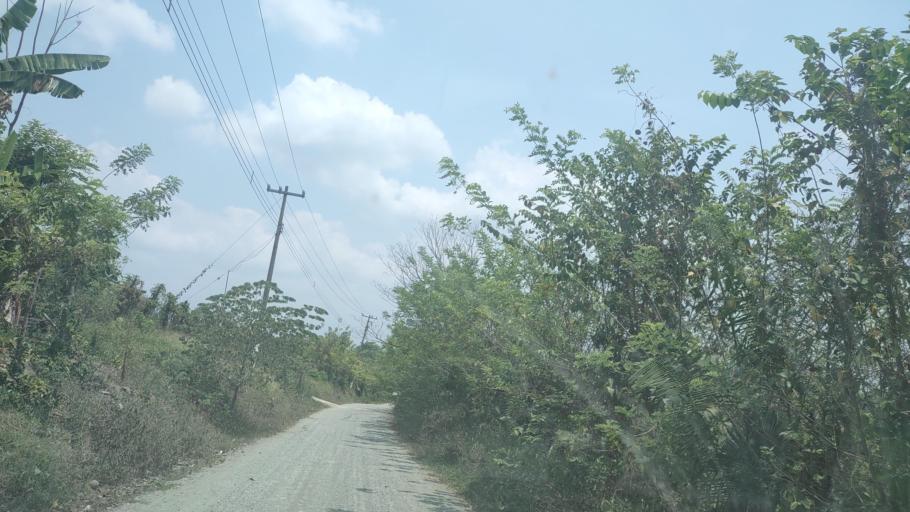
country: MX
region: Tabasco
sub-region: Huimanguillo
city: Francisco Rueda
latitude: 17.5836
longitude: -93.9593
